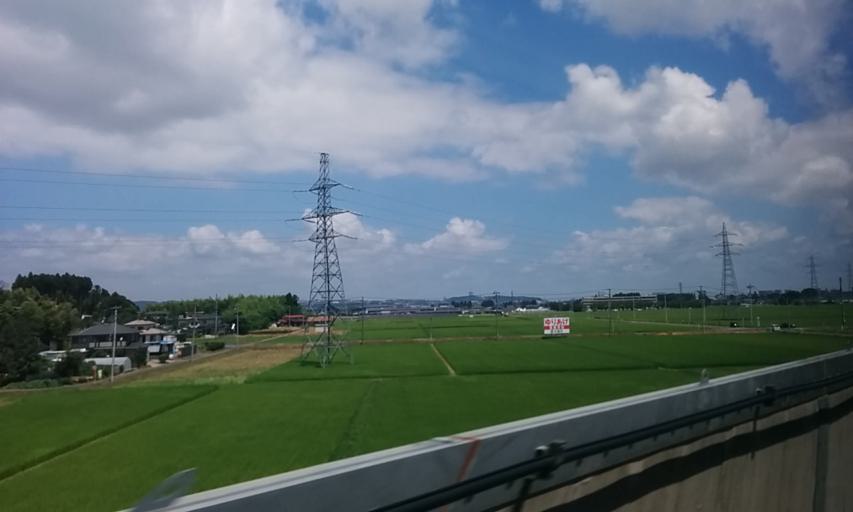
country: JP
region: Miyagi
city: Iwanuma
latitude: 38.1714
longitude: 140.8622
